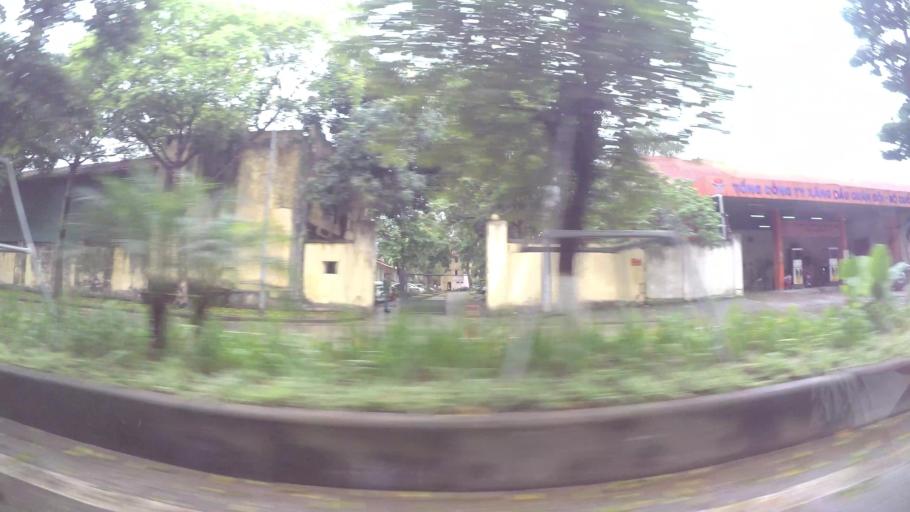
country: VN
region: Ha Noi
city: Hoan Kiem
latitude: 21.0392
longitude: 105.8417
